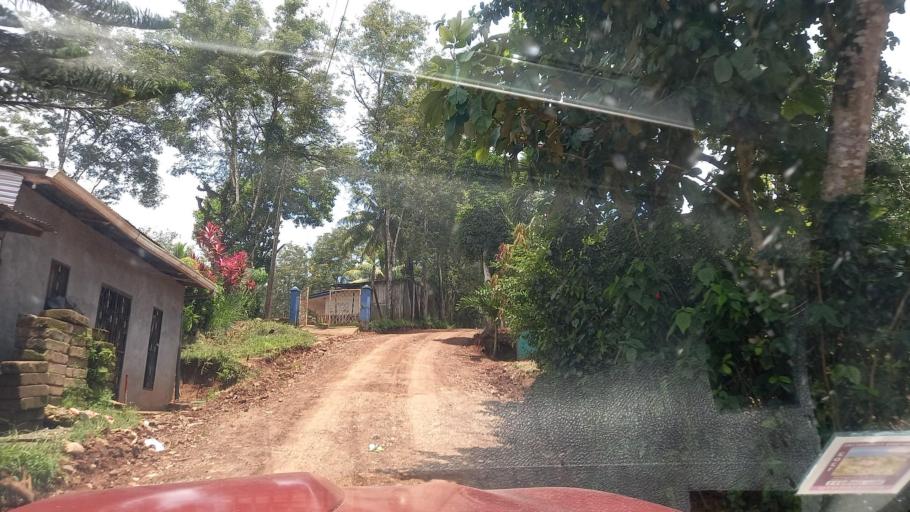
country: NI
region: Atlantico Norte (RAAN)
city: Waslala
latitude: 13.3408
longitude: -85.3704
